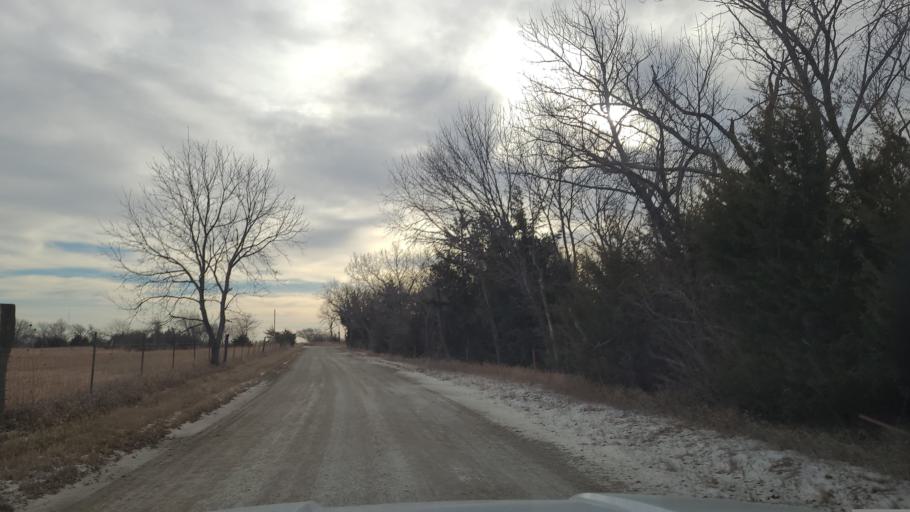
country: US
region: Kansas
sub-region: Shawnee County
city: Topeka
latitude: 39.0446
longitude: -95.4708
